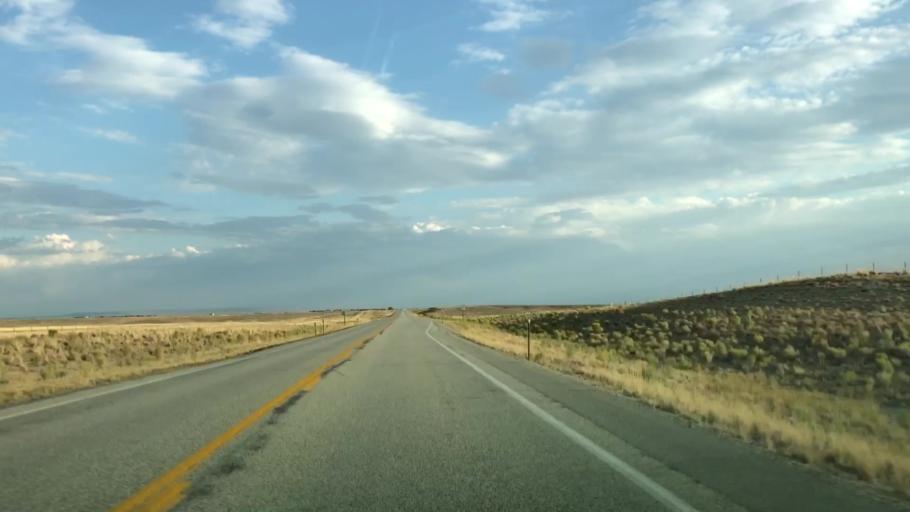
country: US
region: Wyoming
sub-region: Sweetwater County
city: North Rock Springs
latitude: 42.1858
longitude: -109.4793
